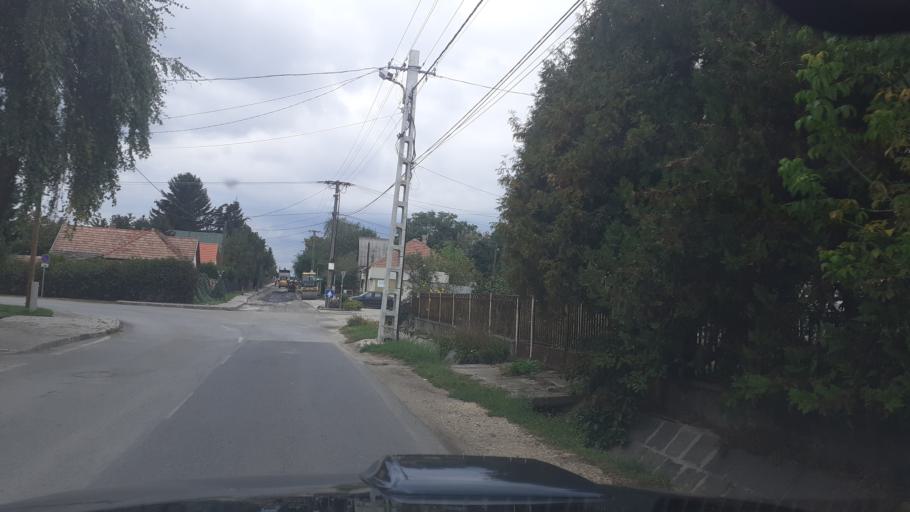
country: HU
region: Fejer
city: Racalmas
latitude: 47.0527
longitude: 18.9196
